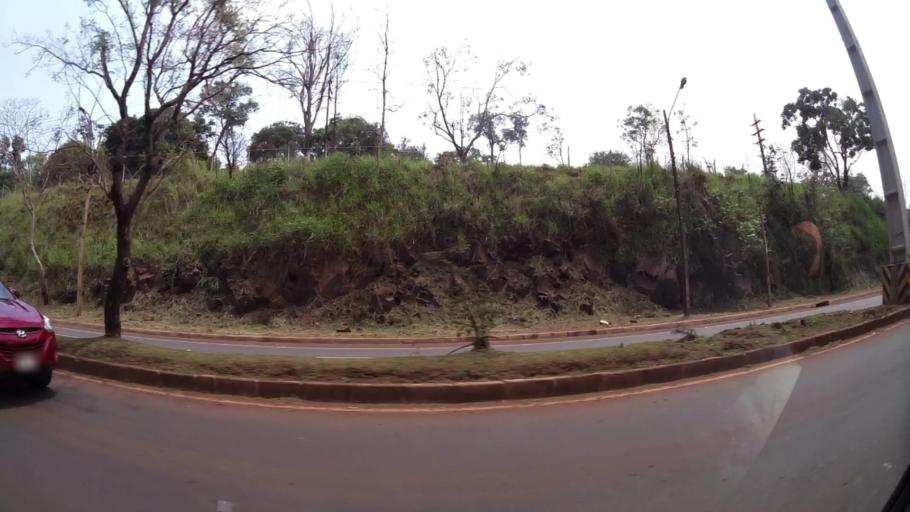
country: PY
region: Alto Parana
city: Ciudad del Este
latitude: -25.4935
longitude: -54.6327
